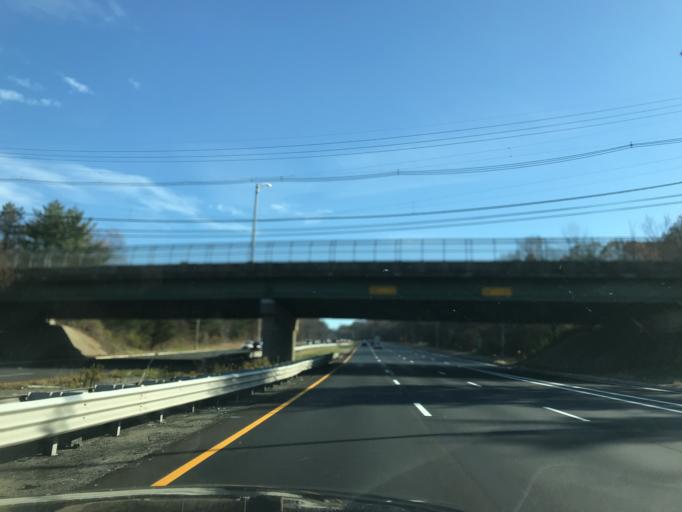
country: US
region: New Jersey
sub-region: Essex County
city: Roseland
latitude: 40.8077
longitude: -74.2881
